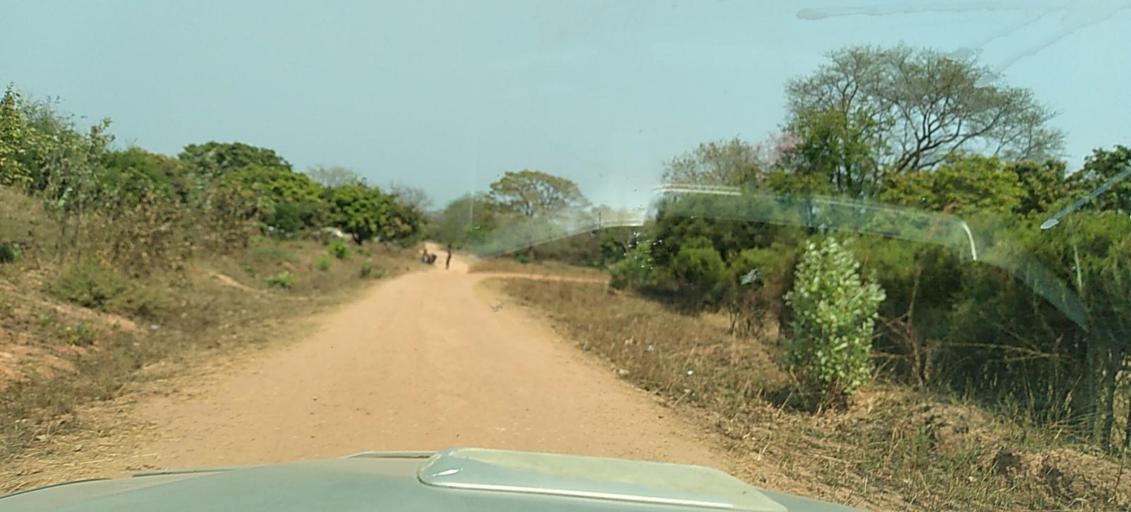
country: ZM
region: North-Western
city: Kasempa
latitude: -13.7078
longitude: 26.3366
